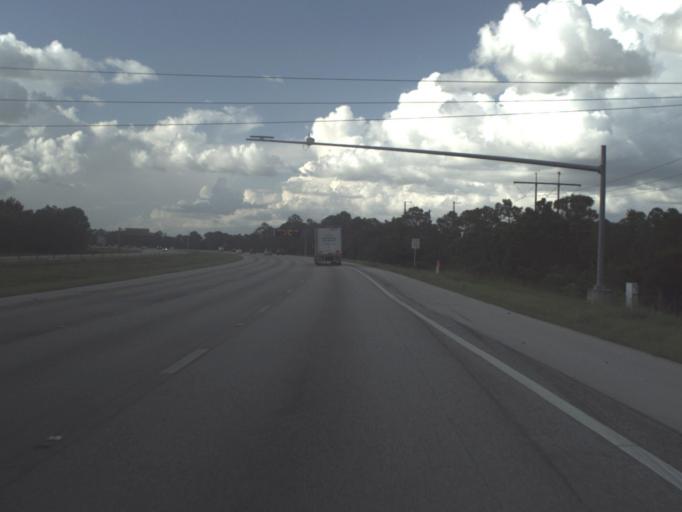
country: US
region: Florida
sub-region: Charlotte County
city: Charlotte Park
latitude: 26.8650
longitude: -81.9724
